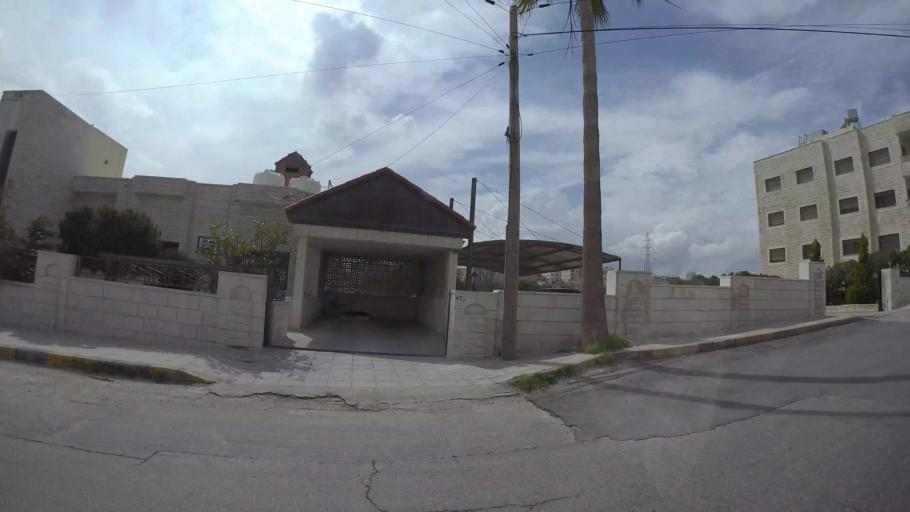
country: JO
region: Amman
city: Amman
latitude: 31.9990
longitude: 35.9339
